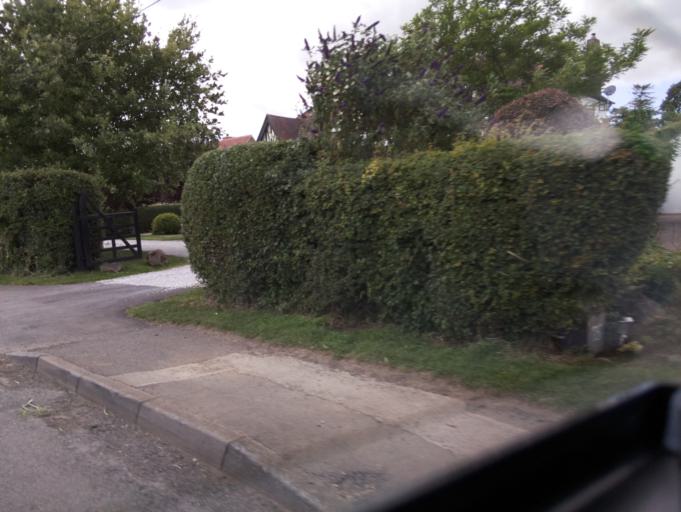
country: GB
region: England
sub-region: Nottinghamshire
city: West Bridgford
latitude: 52.9024
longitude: -1.0914
